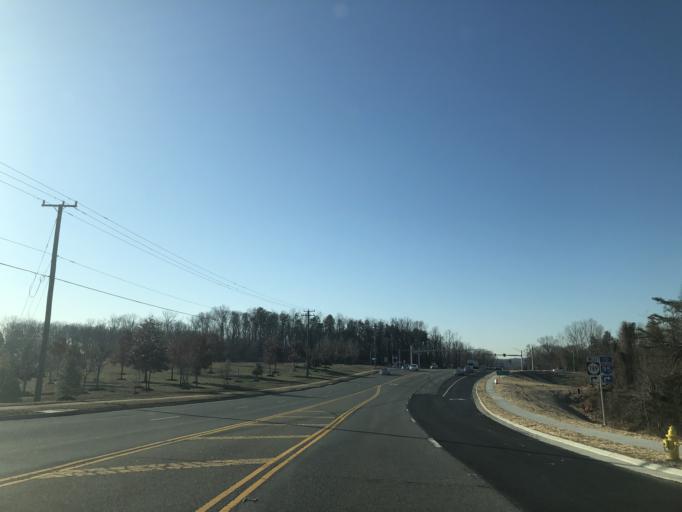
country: US
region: Virginia
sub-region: Stafford County
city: Stafford
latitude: 38.4159
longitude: -77.4093
